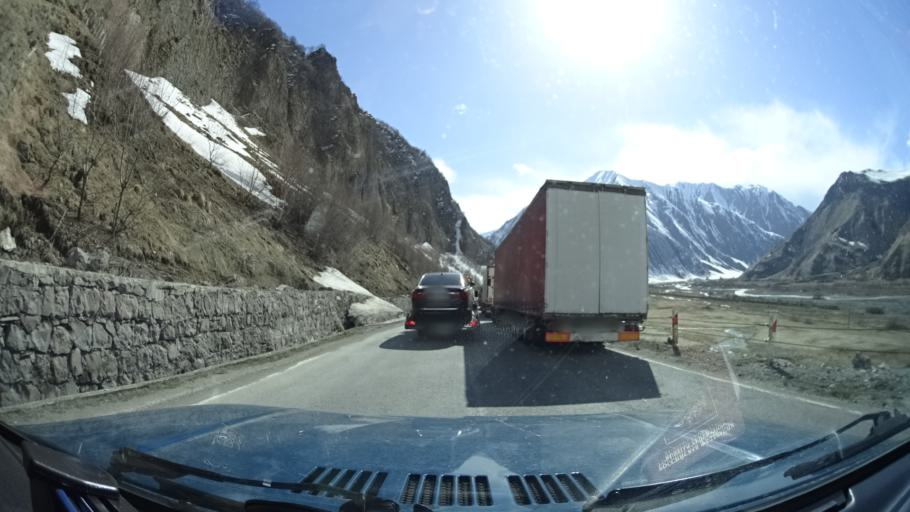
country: GE
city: Gudauri
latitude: 42.5652
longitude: 44.5189
